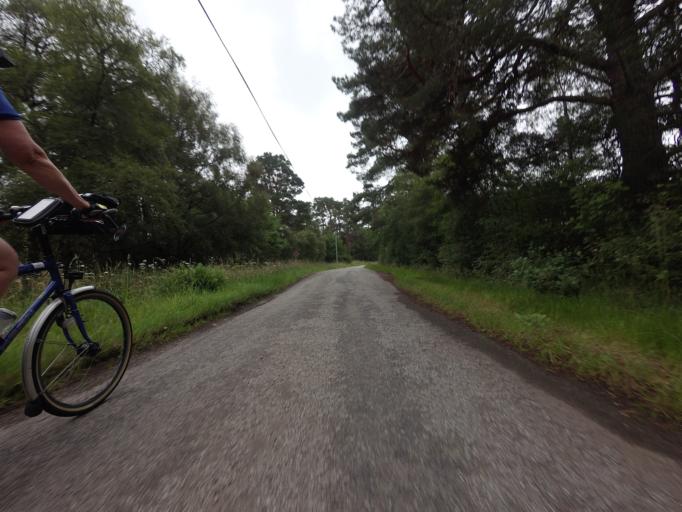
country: GB
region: Scotland
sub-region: Highland
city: Alness
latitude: 57.9889
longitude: -4.4114
